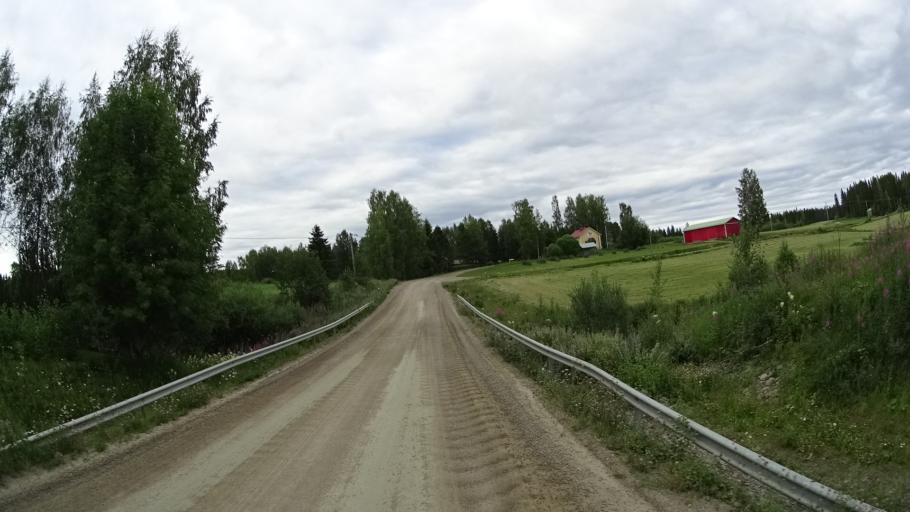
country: FI
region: Satakunta
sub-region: Pohjois-Satakunta
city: Jaemijaervi
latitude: 61.7694
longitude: 22.8465
